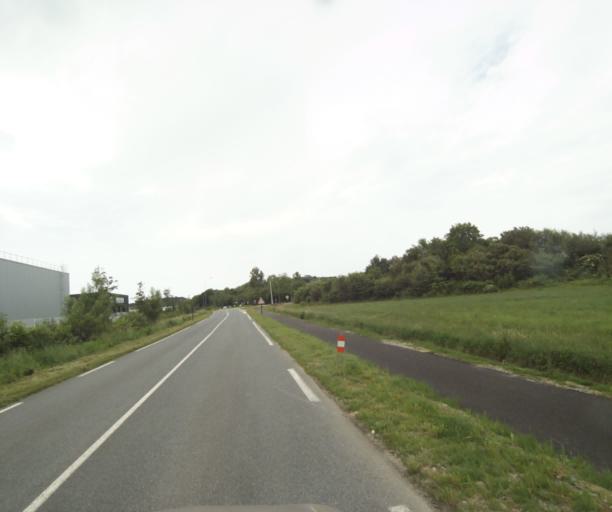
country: FR
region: Aquitaine
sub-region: Departement des Pyrenees-Atlantiques
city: Mouguerre
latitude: 43.4921
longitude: -1.4224
